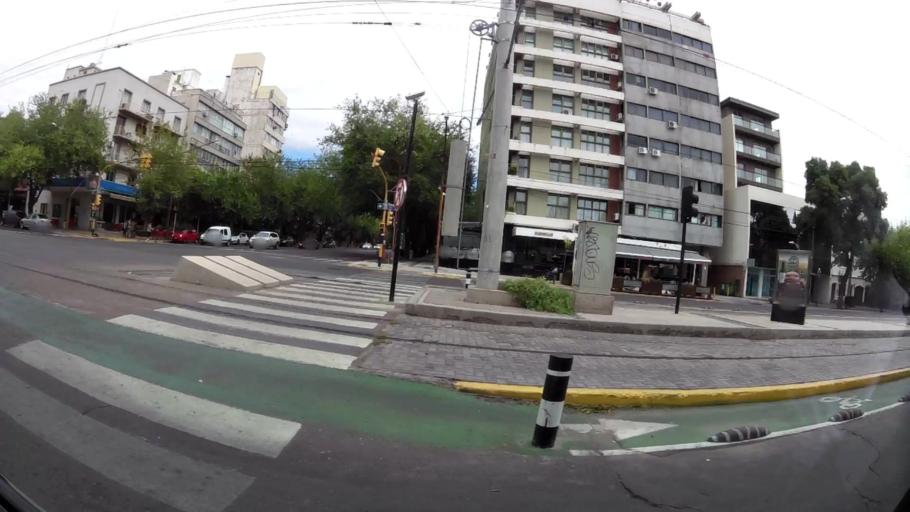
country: AR
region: Mendoza
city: Mendoza
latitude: -32.8884
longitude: -68.8495
